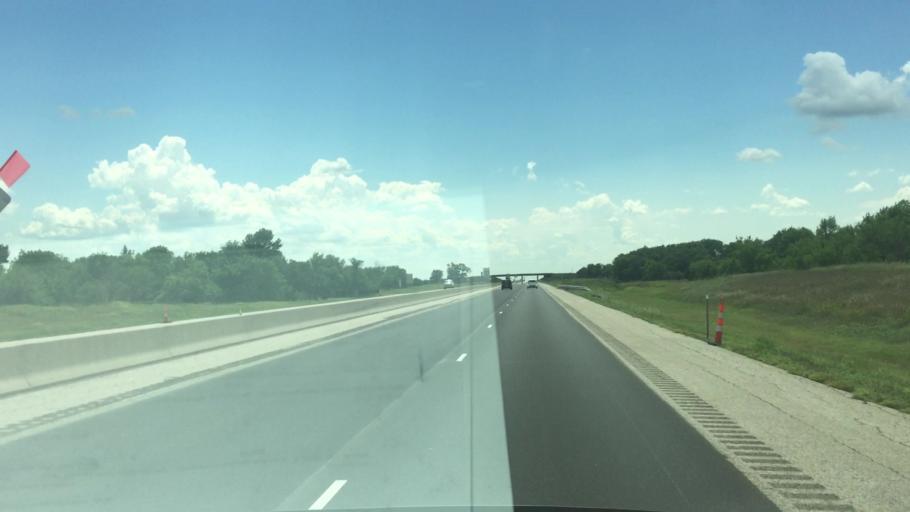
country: US
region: Kansas
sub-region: Osage County
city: Osage City
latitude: 38.7020
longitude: -95.9883
